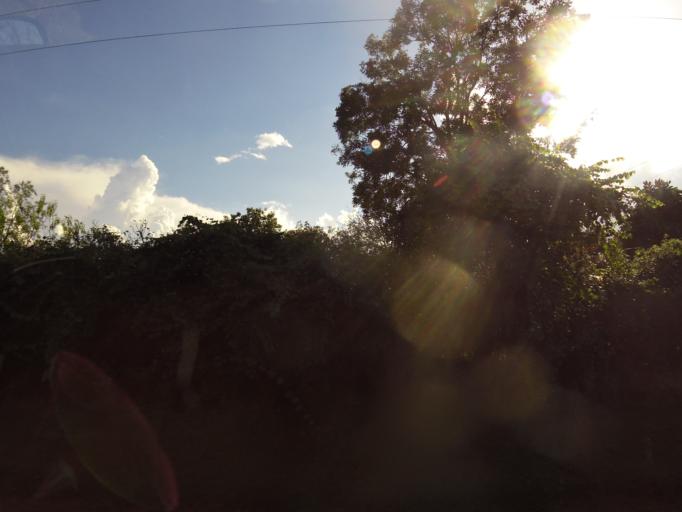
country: US
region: Georgia
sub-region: Brooks County
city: Quitman
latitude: 30.7809
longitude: -83.6193
